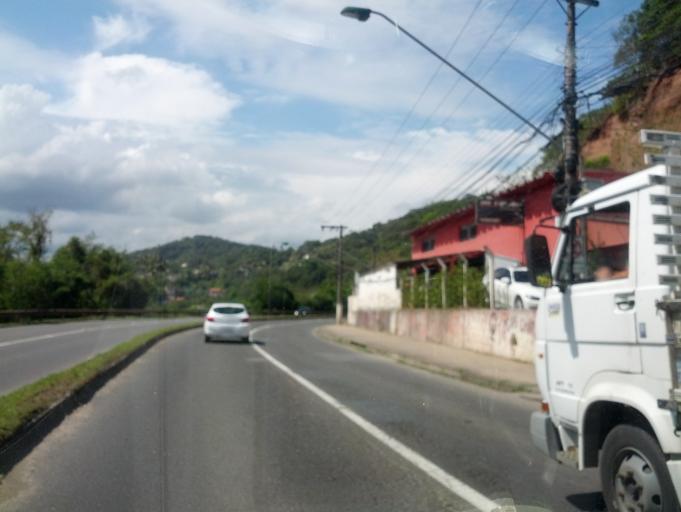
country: BR
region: Santa Catarina
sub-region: Blumenau
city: Blumenau
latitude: -26.9005
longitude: -49.0617
